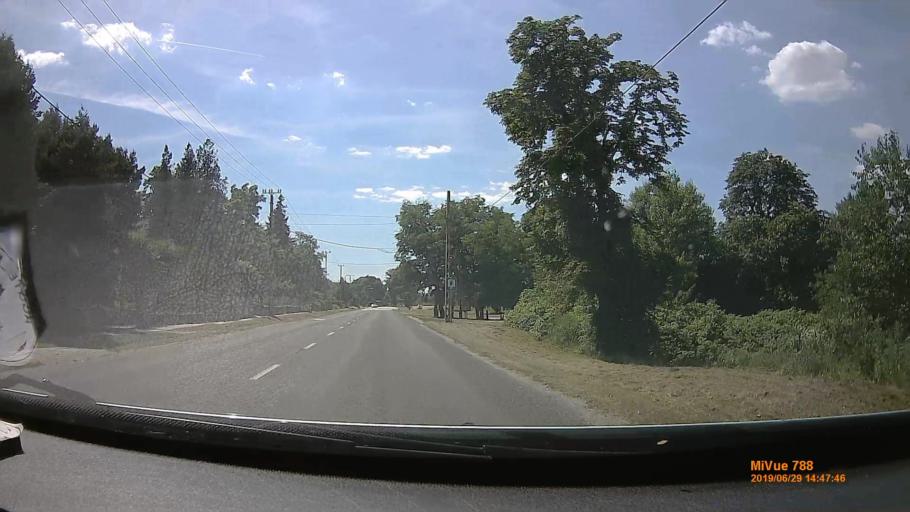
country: HU
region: Komarom-Esztergom
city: Labatlan
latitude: 47.7518
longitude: 18.5159
